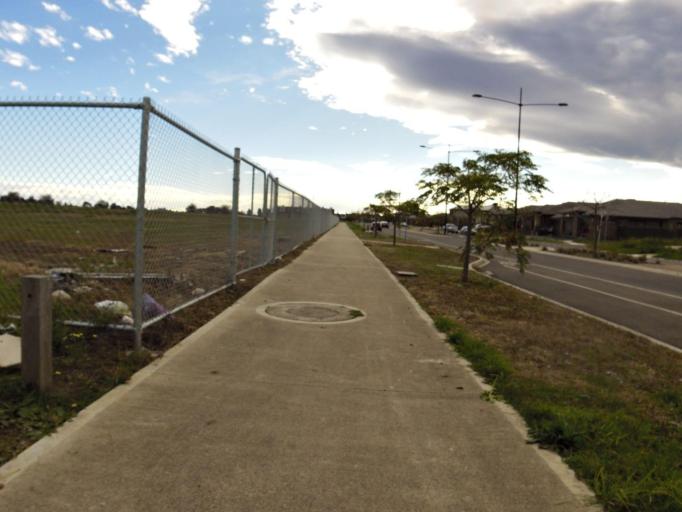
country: AU
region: Victoria
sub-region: Whittlesea
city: Epping
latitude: -37.6183
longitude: 145.0369
